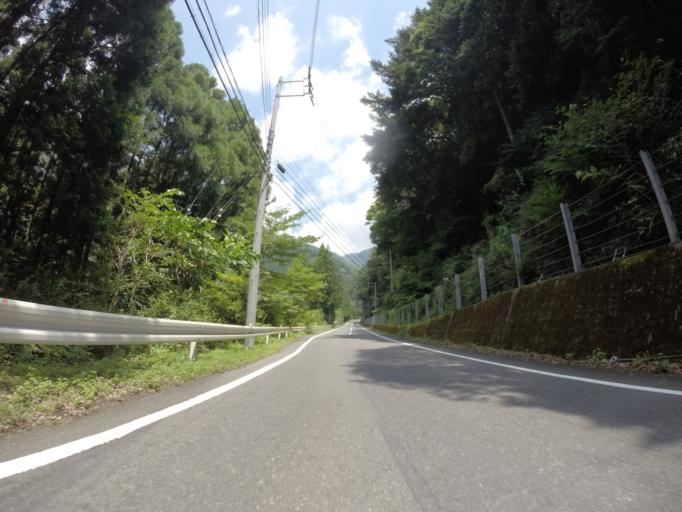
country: JP
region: Shizuoka
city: Fujinomiya
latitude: 35.2684
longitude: 138.3265
